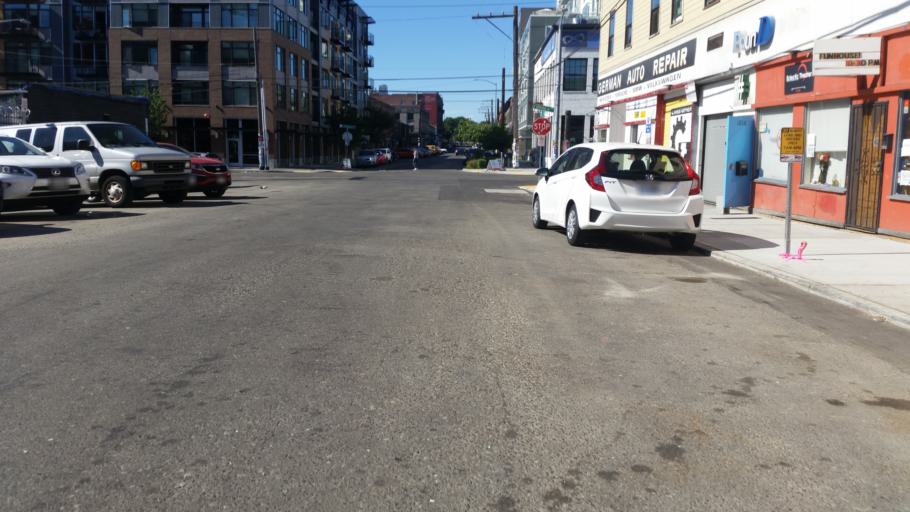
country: US
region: Washington
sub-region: King County
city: Seattle
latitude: 47.6125
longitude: -122.3193
